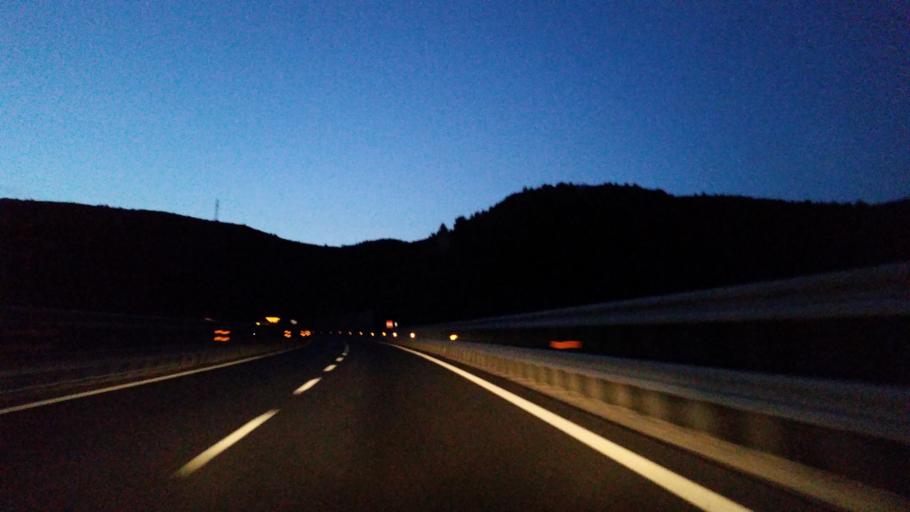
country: IT
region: Liguria
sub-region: Provincia di Savona
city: Laigueglia
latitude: 43.9939
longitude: 8.1367
